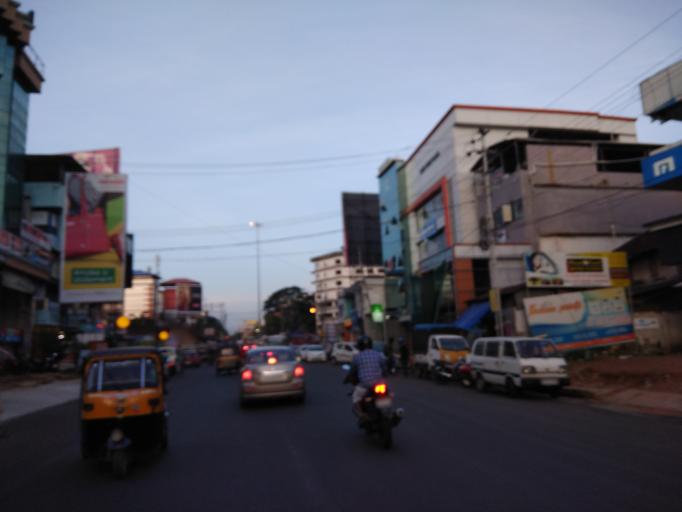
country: IN
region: Kerala
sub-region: Thrissur District
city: Trichur
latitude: 10.5222
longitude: 76.2011
